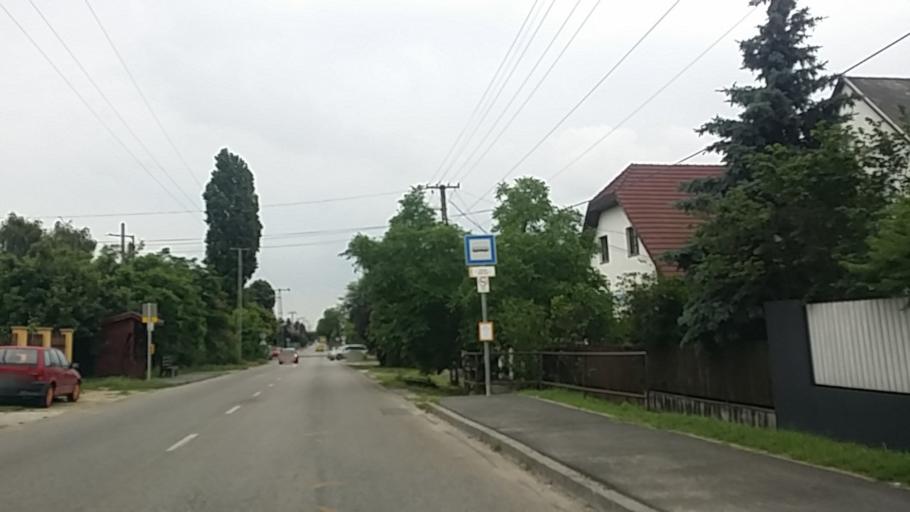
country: HU
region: Pest
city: Gyal
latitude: 47.4139
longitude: 19.2457
